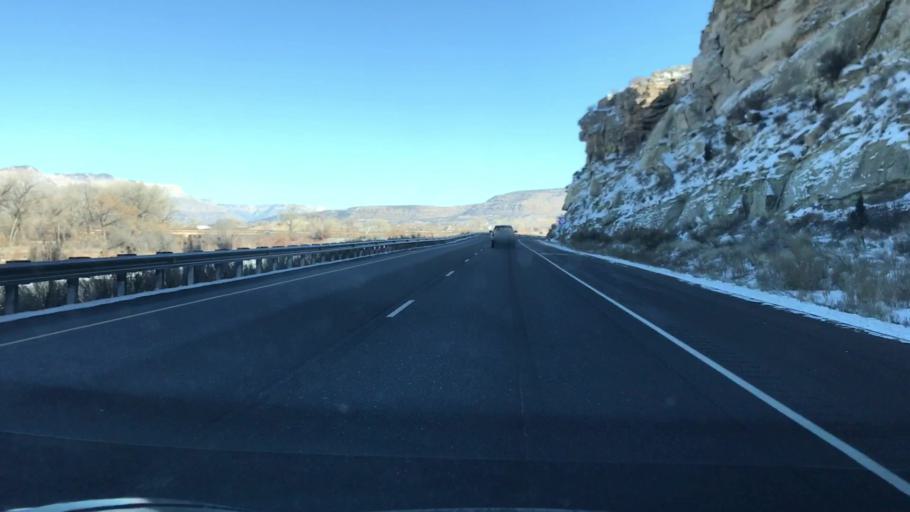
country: US
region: Colorado
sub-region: Mesa County
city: Palisade
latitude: 39.2787
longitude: -108.2383
